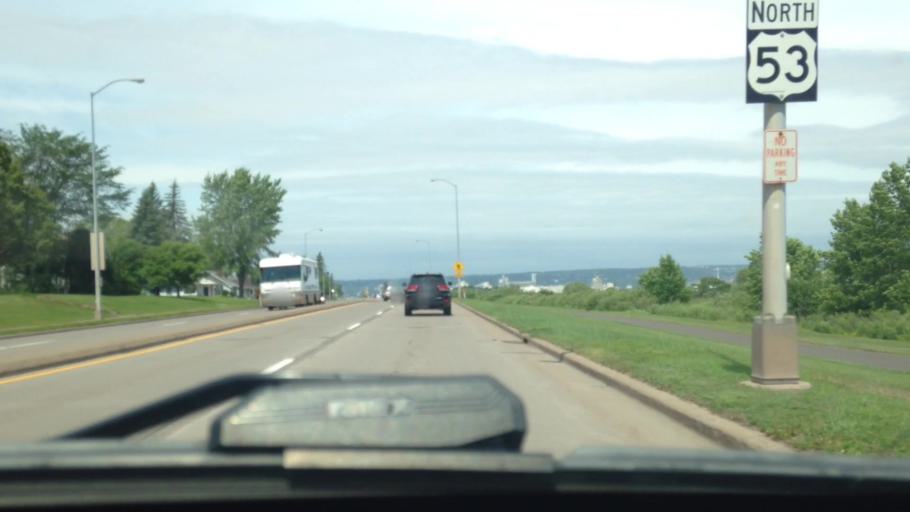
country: US
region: Wisconsin
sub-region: Douglas County
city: Superior
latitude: 46.7164
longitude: -92.0598
